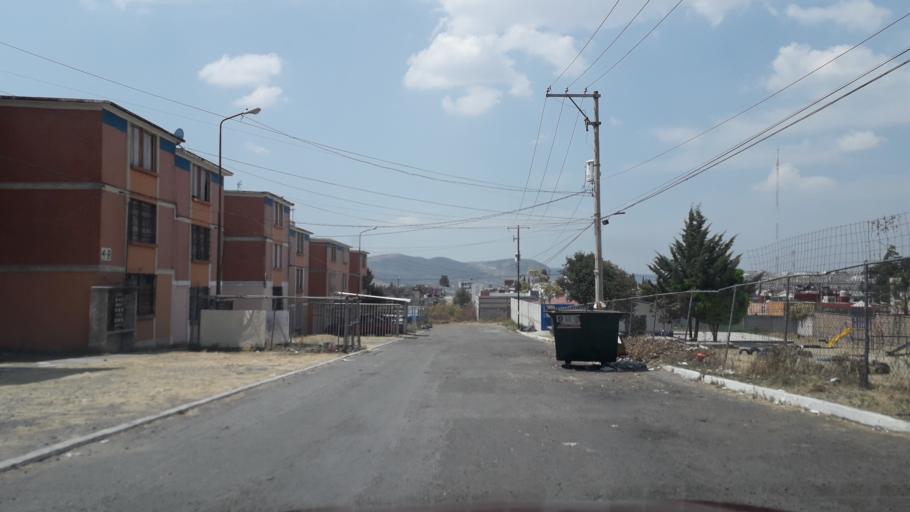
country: MX
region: Puebla
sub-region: Puebla
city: El Capulo (La Quebradora)
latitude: 18.9672
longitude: -98.2647
